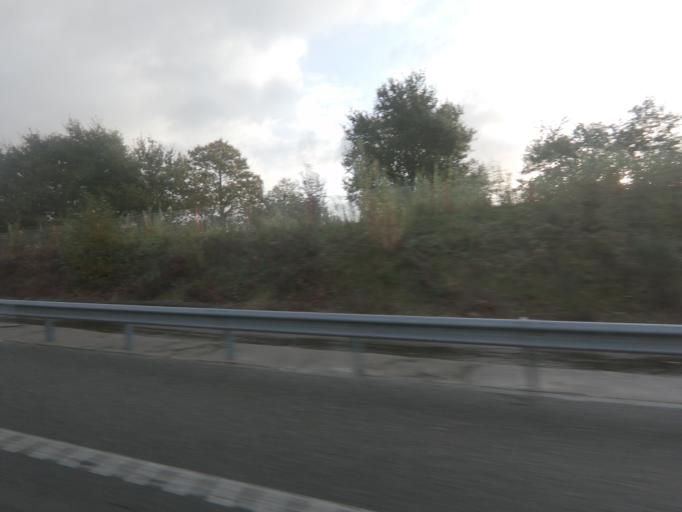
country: ES
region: Galicia
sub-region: Provincia de Pontevedra
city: Porrino
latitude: 42.1717
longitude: -8.6513
